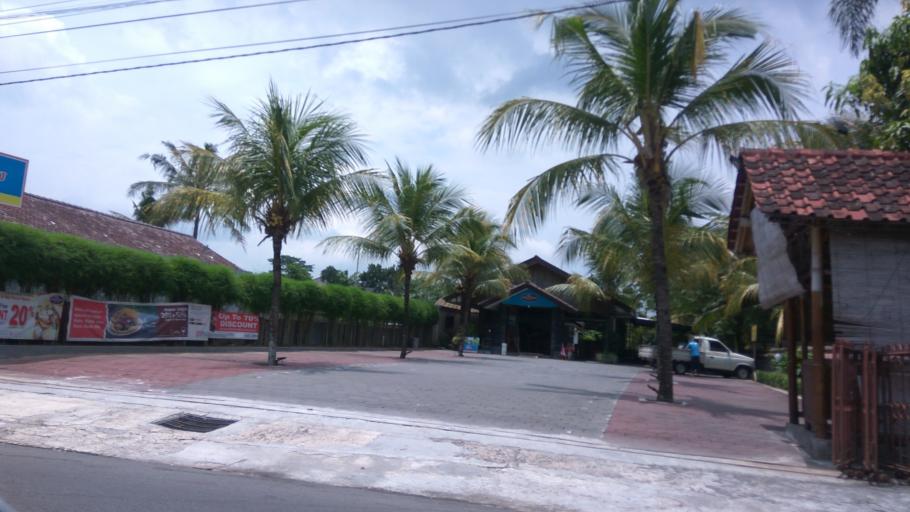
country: ID
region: Daerah Istimewa Yogyakarta
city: Melati
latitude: -7.7273
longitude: 110.3803
